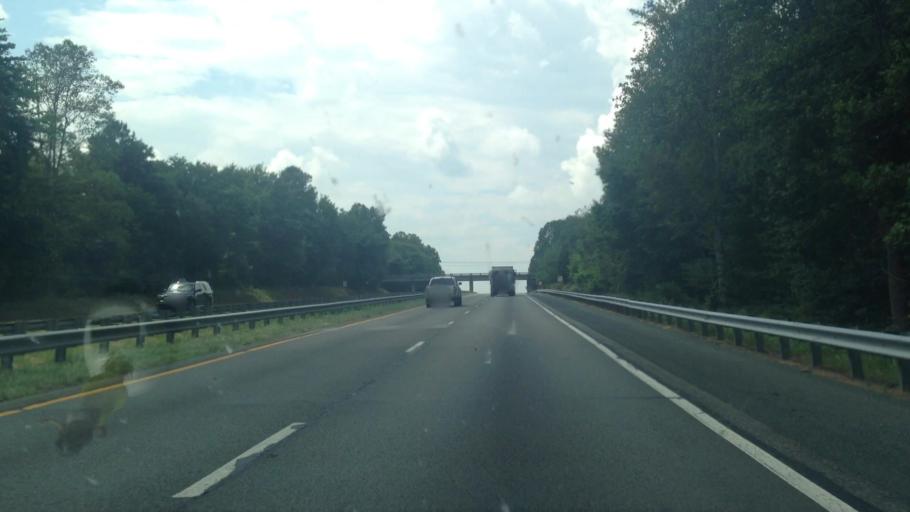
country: US
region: North Carolina
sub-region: Stokes County
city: King
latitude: 36.2815
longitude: -80.3895
